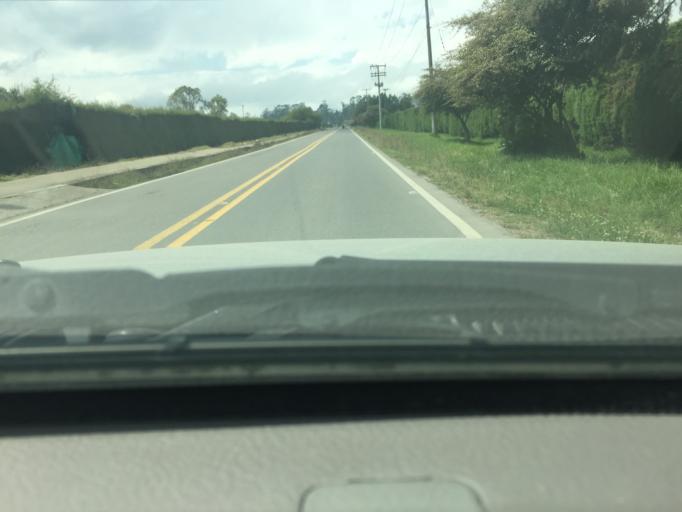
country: CO
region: Cundinamarca
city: Bojaca
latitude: 4.7702
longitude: -74.3213
